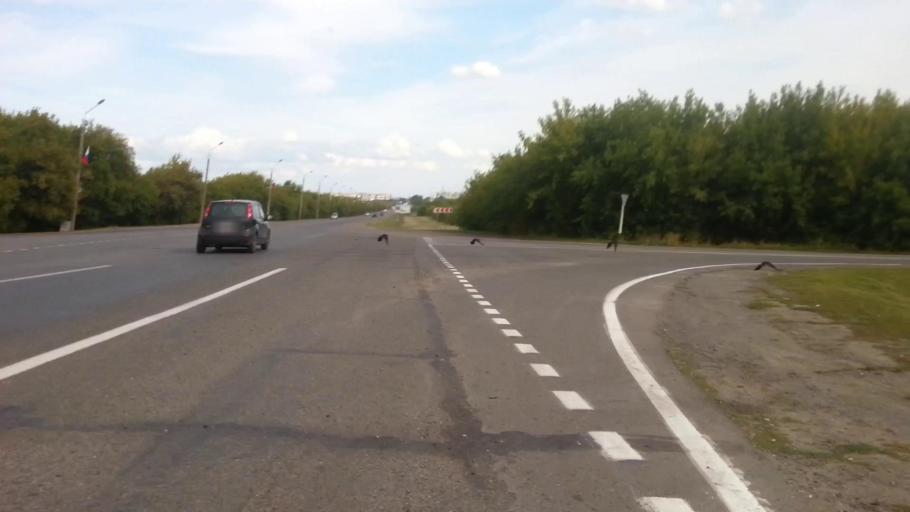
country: RU
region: Altai Krai
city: Novosilikatnyy
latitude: 53.3508
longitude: 83.5955
